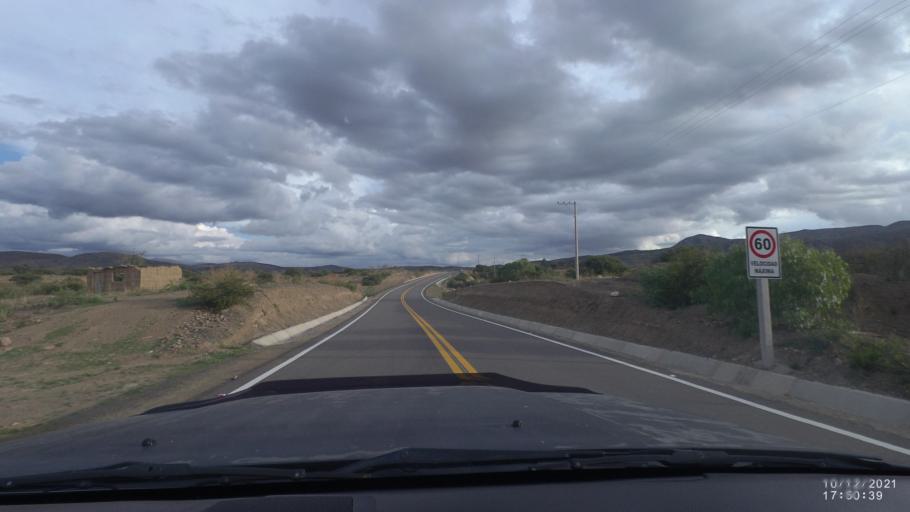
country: BO
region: Cochabamba
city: Tarata
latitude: -17.6686
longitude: -65.9626
